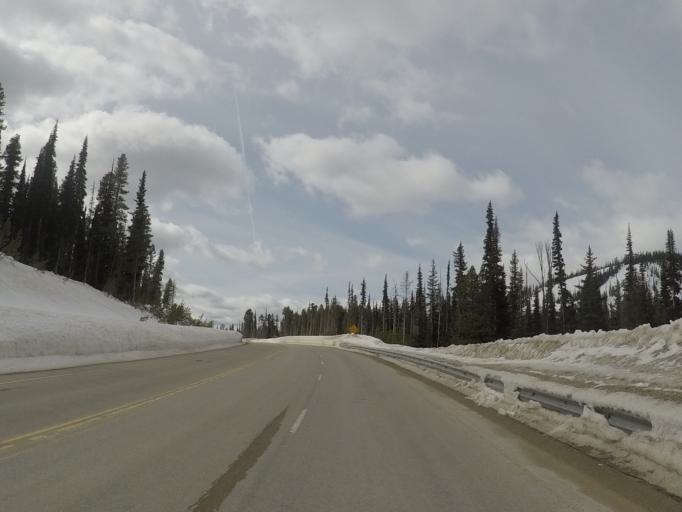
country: US
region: Idaho
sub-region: Lemhi County
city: Salmon
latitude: 45.6972
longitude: -113.9481
